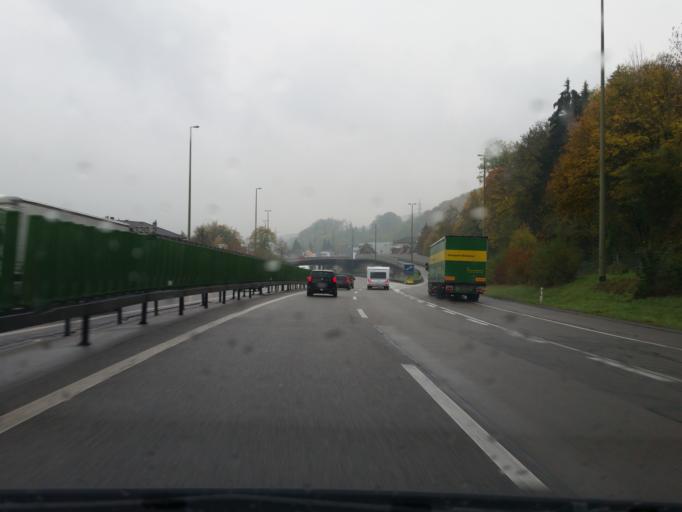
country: CH
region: Zurich
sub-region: Bezirk Winterthur
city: Toess (Kreis 4) / Schlosstal
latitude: 47.4904
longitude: 8.7021
